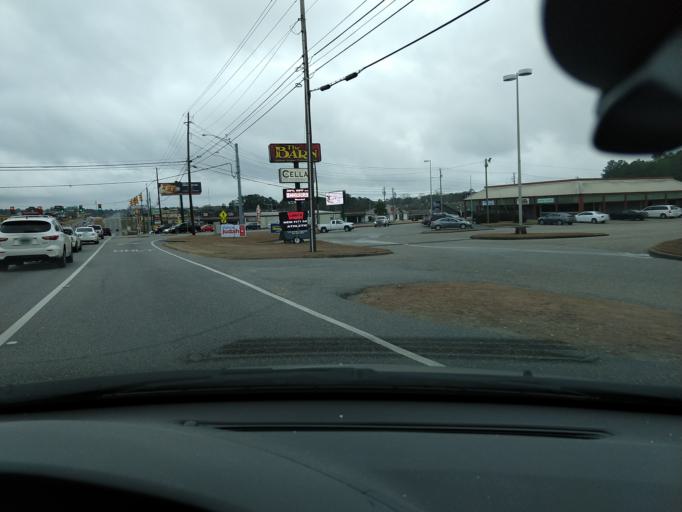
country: US
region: Alabama
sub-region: Houston County
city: Dothan
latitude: 31.2577
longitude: -85.4342
